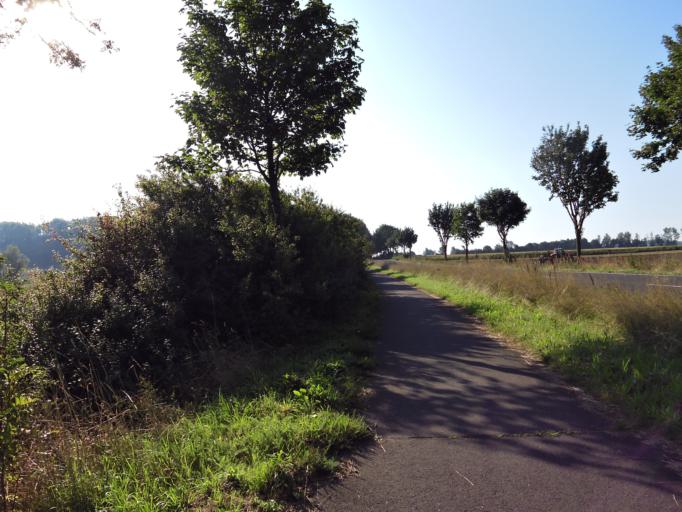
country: DE
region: North Rhine-Westphalia
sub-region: Regierungsbezirk Koln
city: Alsdorf
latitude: 50.8910
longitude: 6.1440
